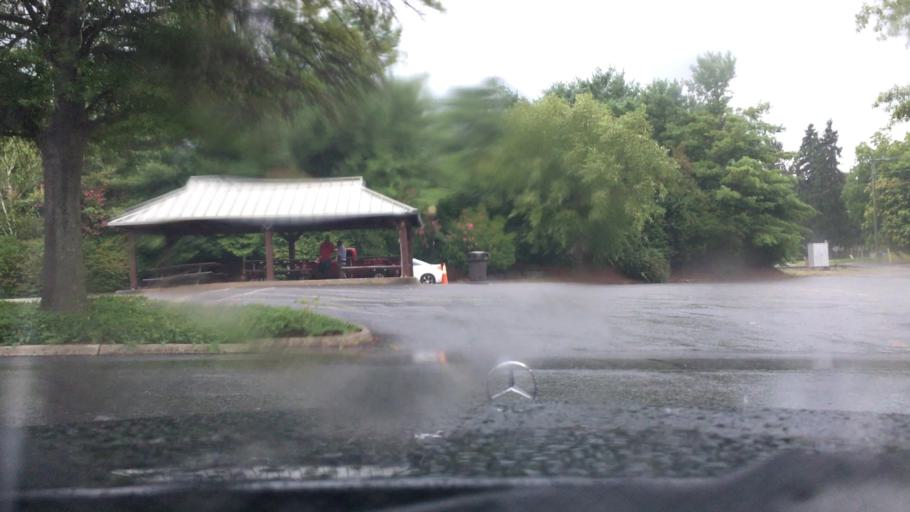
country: US
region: Virginia
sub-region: Campbell County
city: Altavista
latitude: 37.1094
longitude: -79.2914
